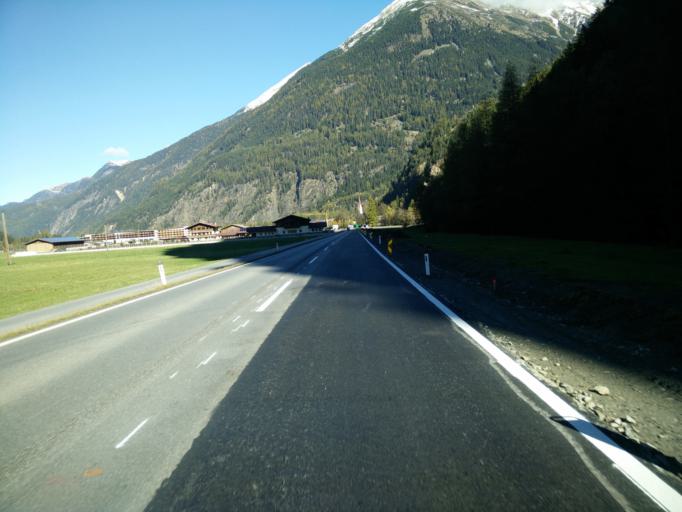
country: AT
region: Tyrol
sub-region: Politischer Bezirk Imst
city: Umhausen
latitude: 47.0606
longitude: 10.9656
